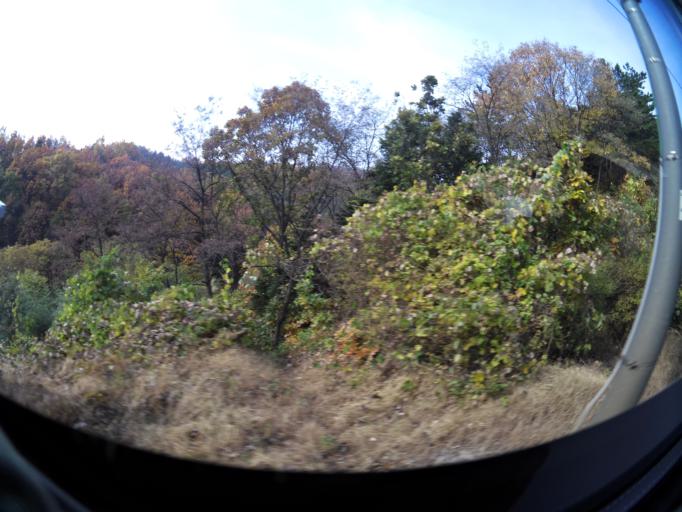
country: KR
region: Gyeongsangbuk-do
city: Gimcheon
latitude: 36.1829
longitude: 128.0084
